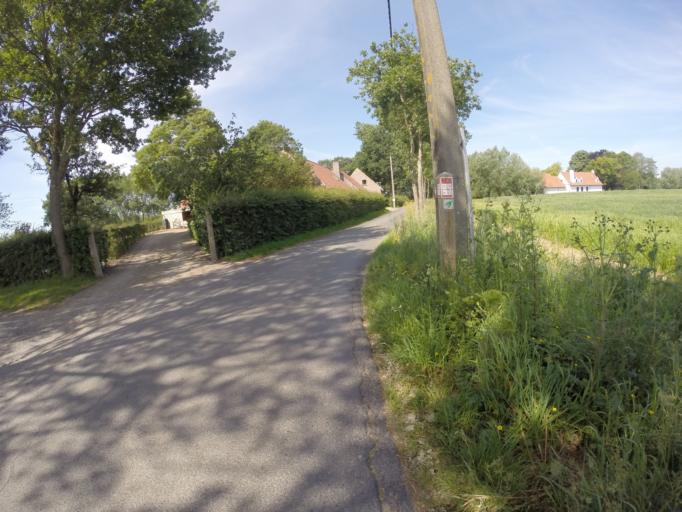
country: BE
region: Flanders
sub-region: Provincie West-Vlaanderen
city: Beernem
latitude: 51.1585
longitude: 3.3345
